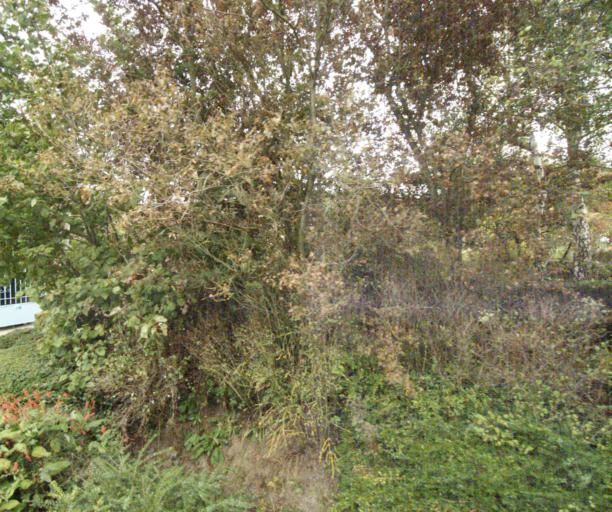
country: FR
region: Nord-Pas-de-Calais
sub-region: Departement du Nord
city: Erquinghem-Lys
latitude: 50.6735
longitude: 2.8201
